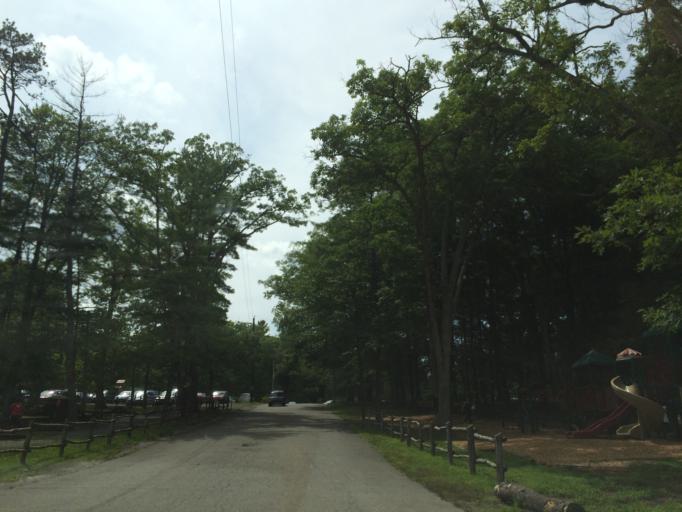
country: US
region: Pennsylvania
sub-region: Pike County
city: Saw Creek
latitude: 41.1171
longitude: -75.0057
